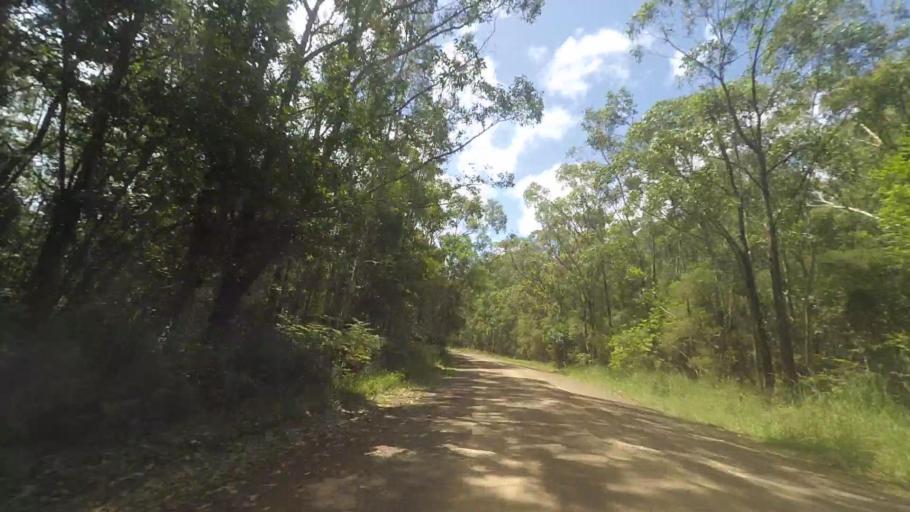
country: AU
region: New South Wales
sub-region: Great Lakes
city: Bulahdelah
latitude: -32.4926
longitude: 152.2762
